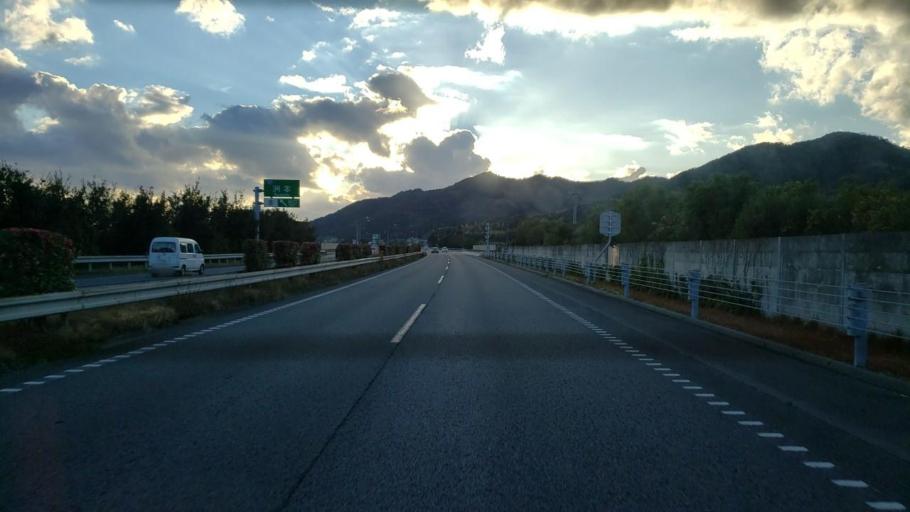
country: JP
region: Hyogo
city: Sumoto
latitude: 34.3449
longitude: 134.8443
